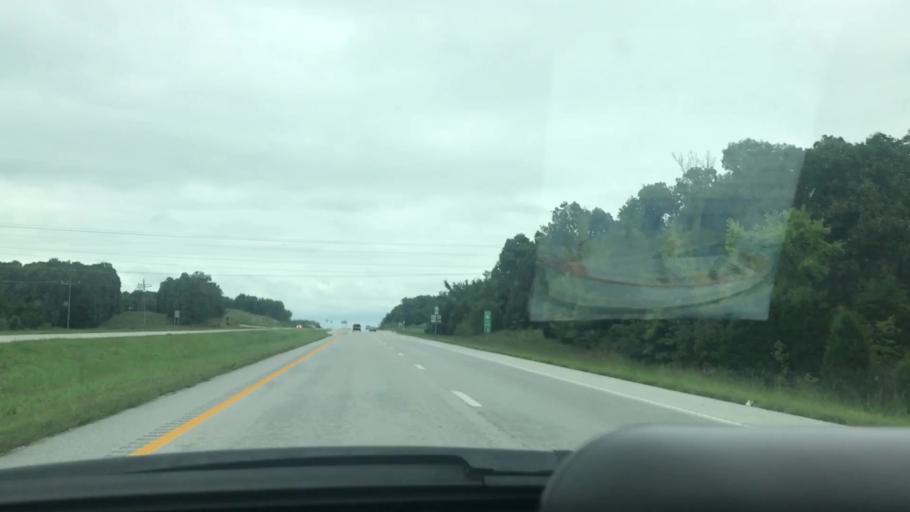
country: US
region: Missouri
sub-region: Greene County
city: Fair Grove
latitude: 37.3251
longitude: -93.1680
